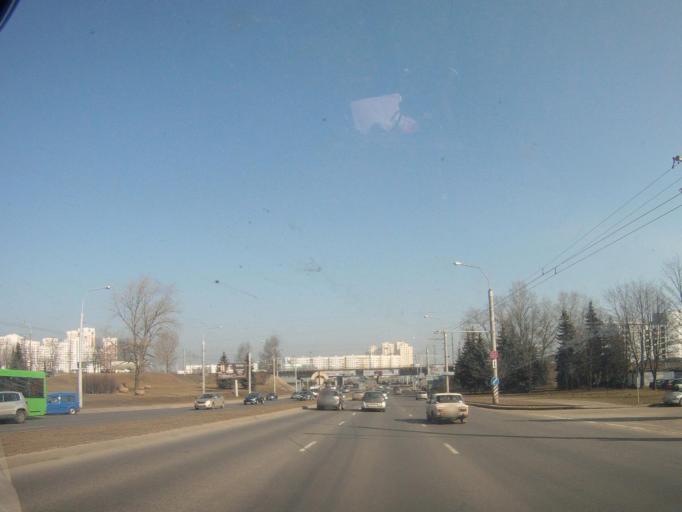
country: BY
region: Minsk
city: Novoye Medvezhino
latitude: 53.9248
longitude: 27.5035
